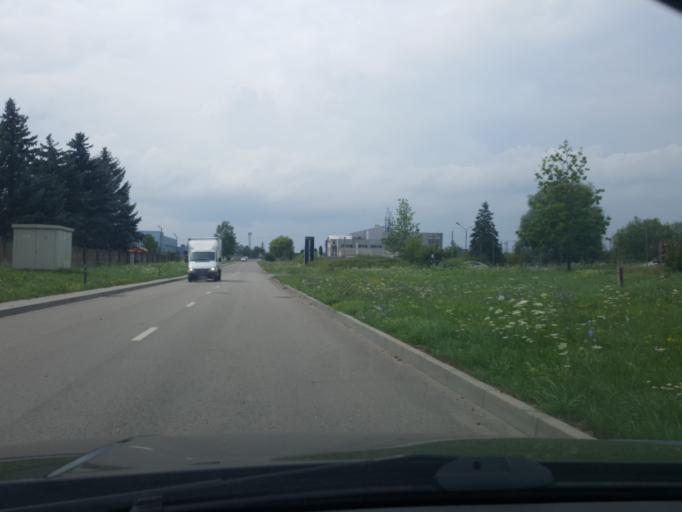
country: LT
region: Alytaus apskritis
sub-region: Alytus
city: Alytus
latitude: 54.4376
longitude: 24.0220
